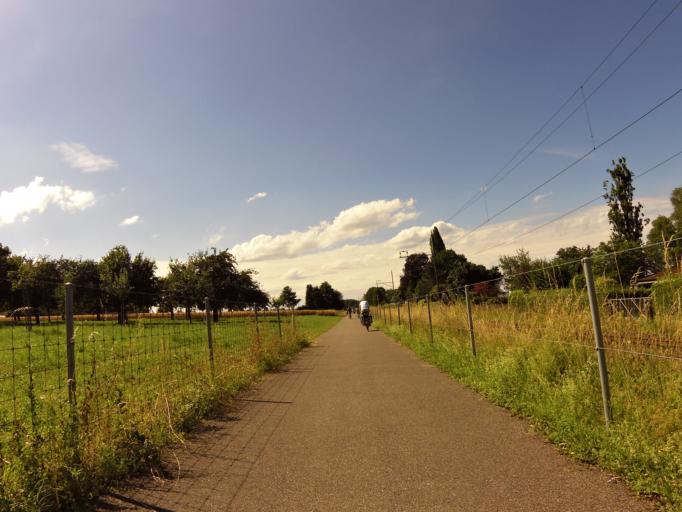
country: CH
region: Thurgau
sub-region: Arbon District
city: Arbon
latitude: 47.5306
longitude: 9.4110
